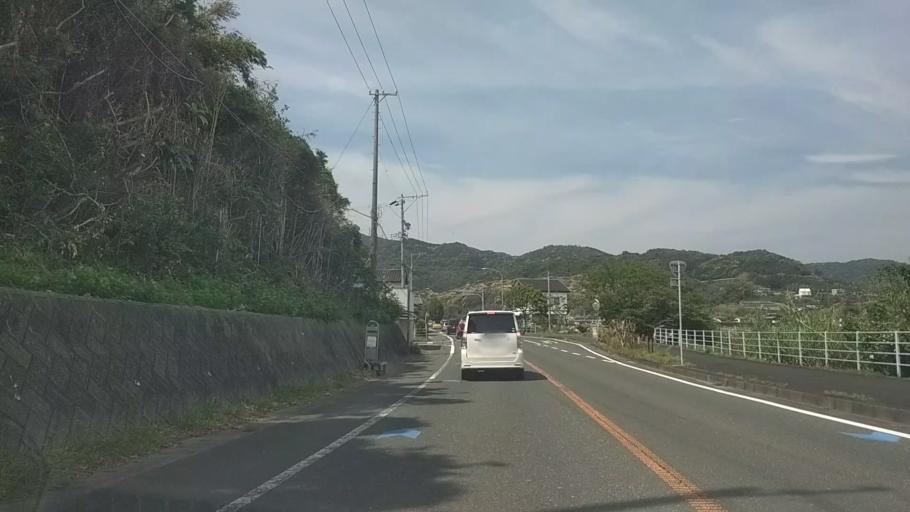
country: JP
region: Shizuoka
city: Kosai-shi
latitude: 34.7956
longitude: 137.6203
